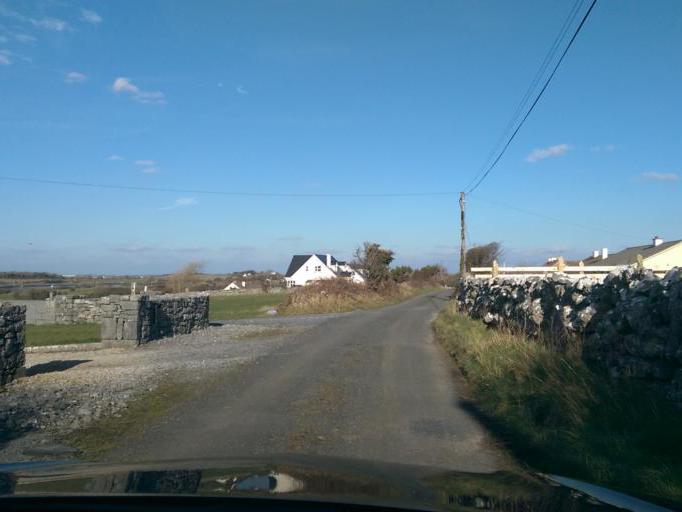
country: IE
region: Connaught
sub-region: County Galway
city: Oranmore
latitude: 53.2326
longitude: -8.9752
